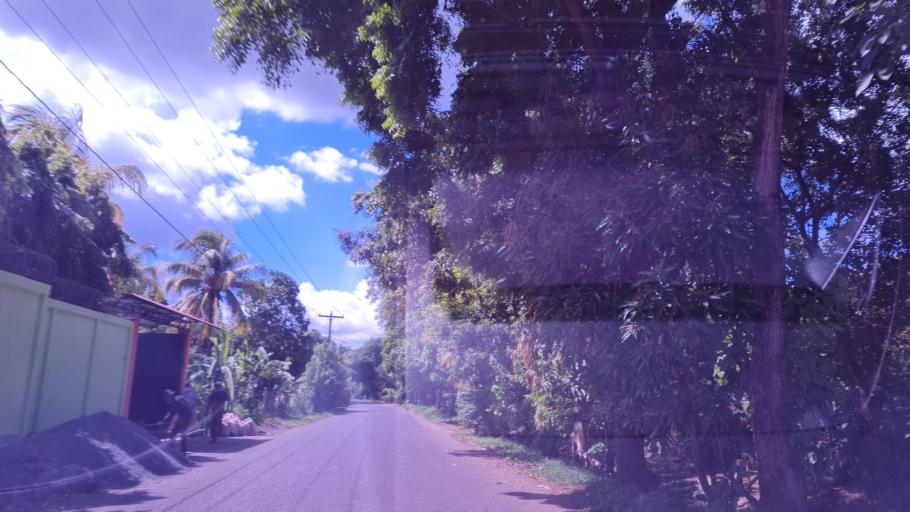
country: NI
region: Masaya
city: Nindiri
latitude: 12.0166
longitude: -86.1182
